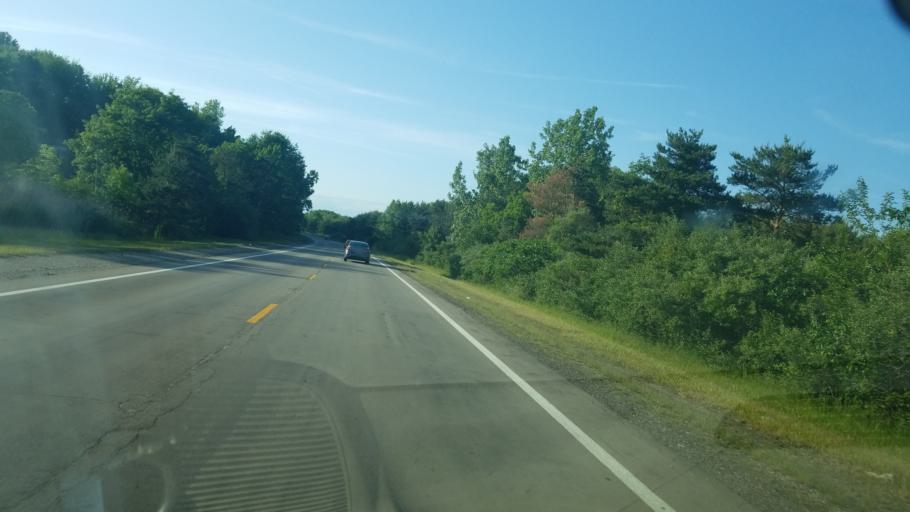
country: US
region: Ohio
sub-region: Portage County
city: Kent
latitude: 41.1474
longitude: -81.3197
